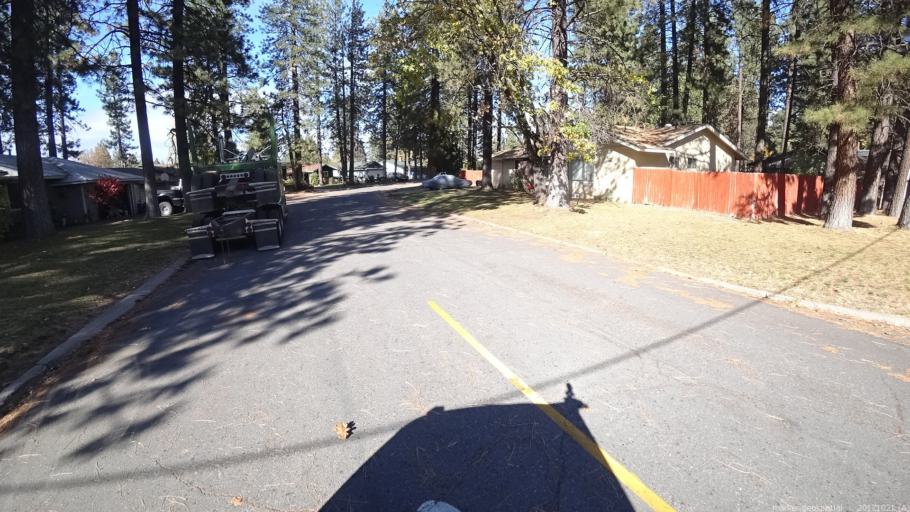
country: US
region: California
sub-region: Shasta County
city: Burney
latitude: 40.8852
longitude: -121.6546
